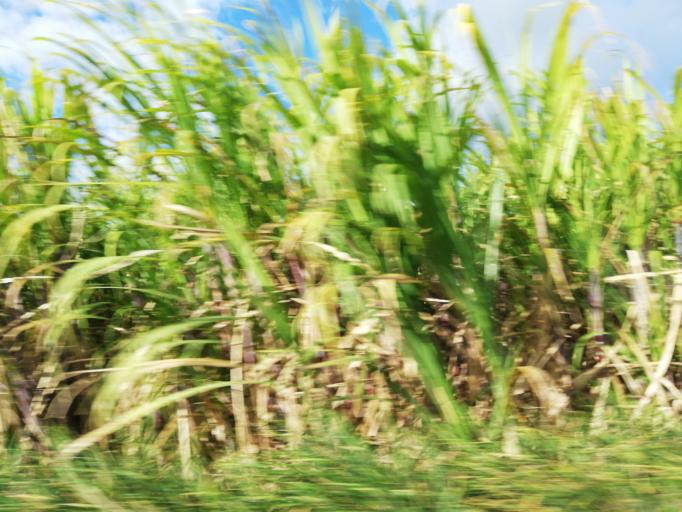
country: MU
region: Flacq
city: Olivia
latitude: -20.3120
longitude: 57.7128
